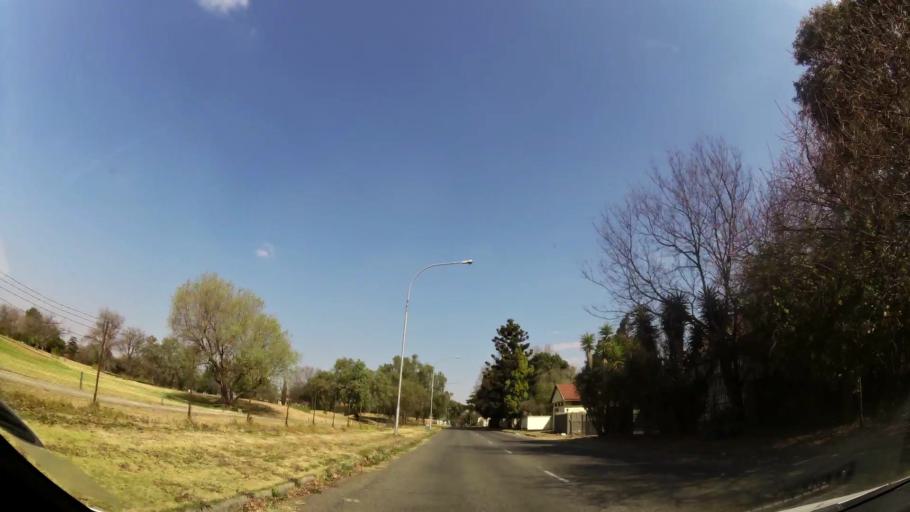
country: ZA
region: Gauteng
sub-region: Ekurhuleni Metropolitan Municipality
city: Benoni
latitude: -26.1847
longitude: 28.2918
